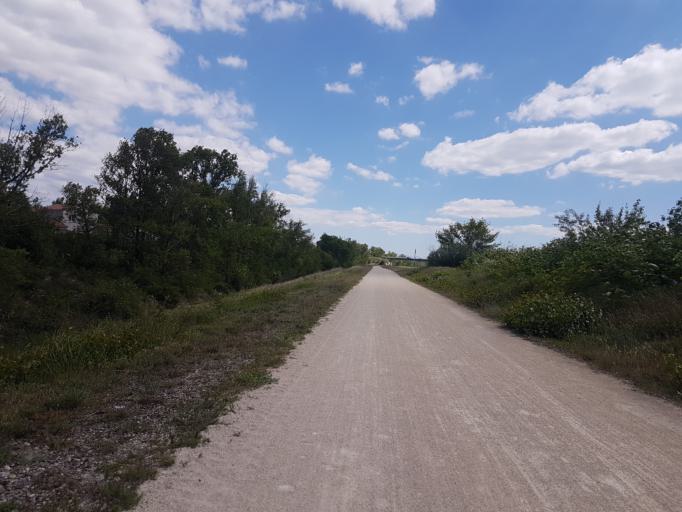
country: FR
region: Rhone-Alpes
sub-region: Departement de la Drome
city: La Roche-de-Glun
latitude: 45.0186
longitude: 4.8511
